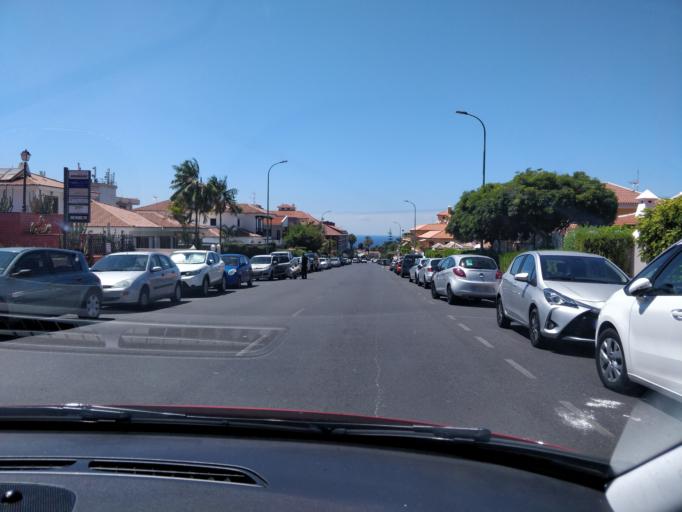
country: ES
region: Canary Islands
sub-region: Provincia de Santa Cruz de Tenerife
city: Puerto de la Cruz
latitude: 28.4122
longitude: -16.5356
